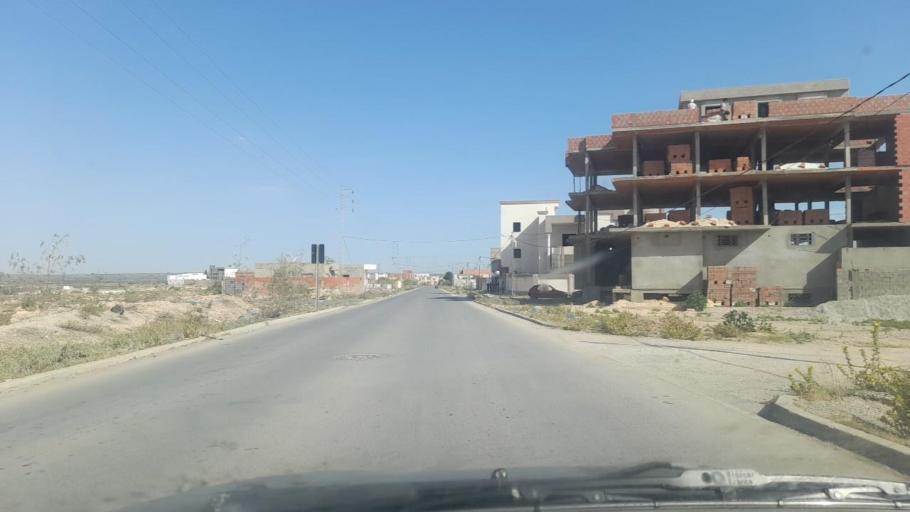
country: TN
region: Susah
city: Akouda
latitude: 35.8136
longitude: 10.5591
